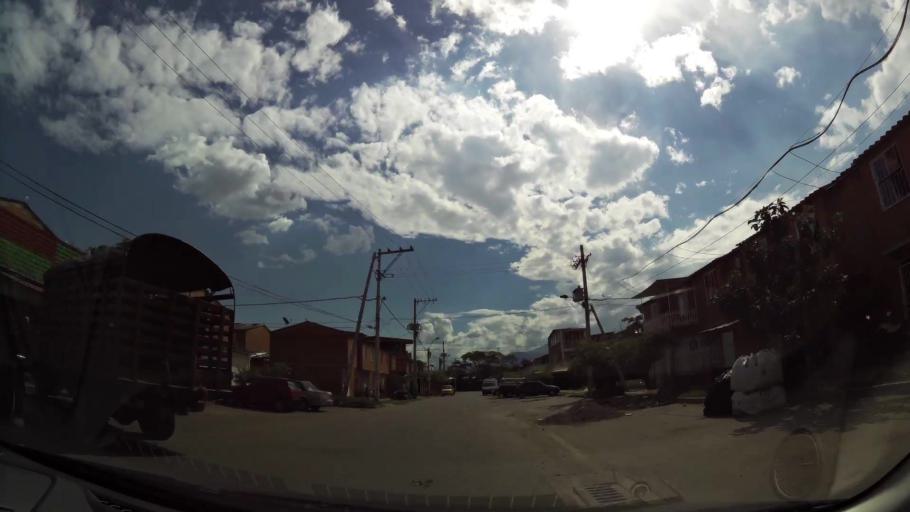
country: CO
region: Valle del Cauca
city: Cali
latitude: 3.3908
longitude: -76.5089
